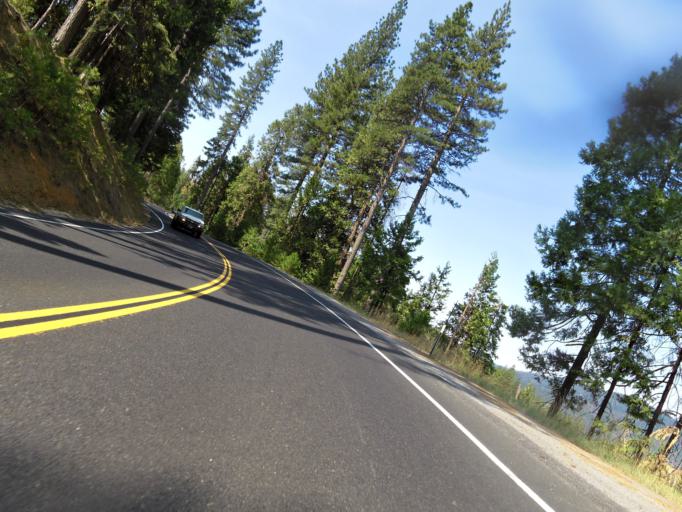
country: US
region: California
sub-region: Tuolumne County
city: Twain Harte
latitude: 38.0649
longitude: -120.1951
